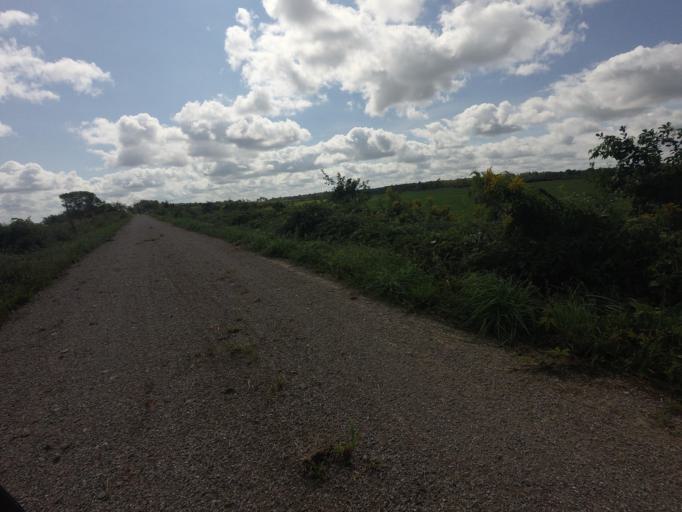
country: CA
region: Ontario
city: Huron East
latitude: 43.6420
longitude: -81.2067
